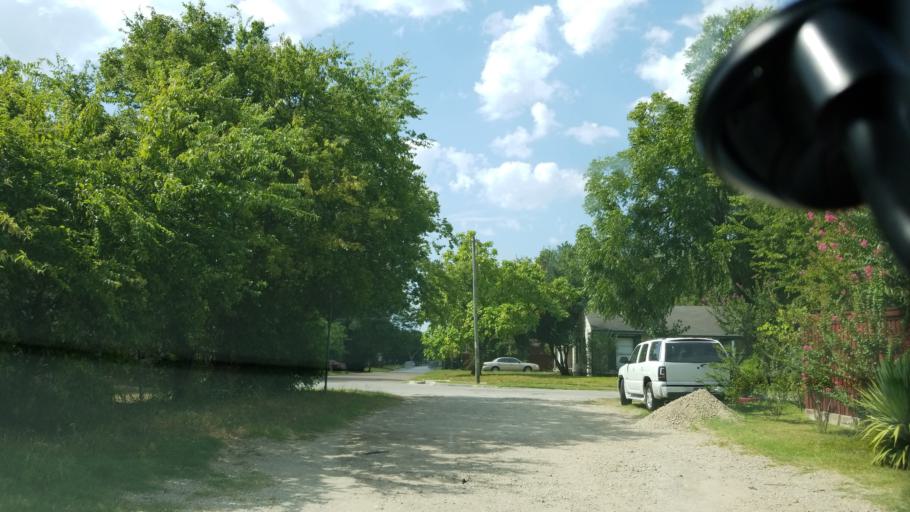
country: US
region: Texas
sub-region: Dallas County
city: Grand Prairie
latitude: 32.7520
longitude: -96.9925
